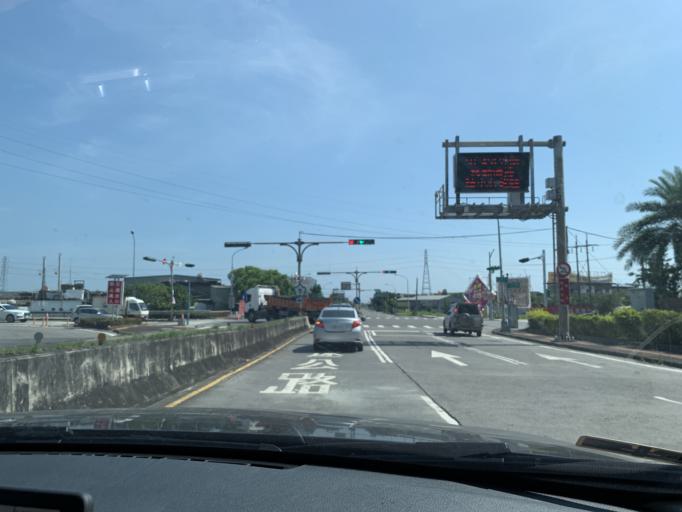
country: TW
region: Taiwan
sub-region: Yilan
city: Yilan
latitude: 24.6164
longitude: 121.8264
